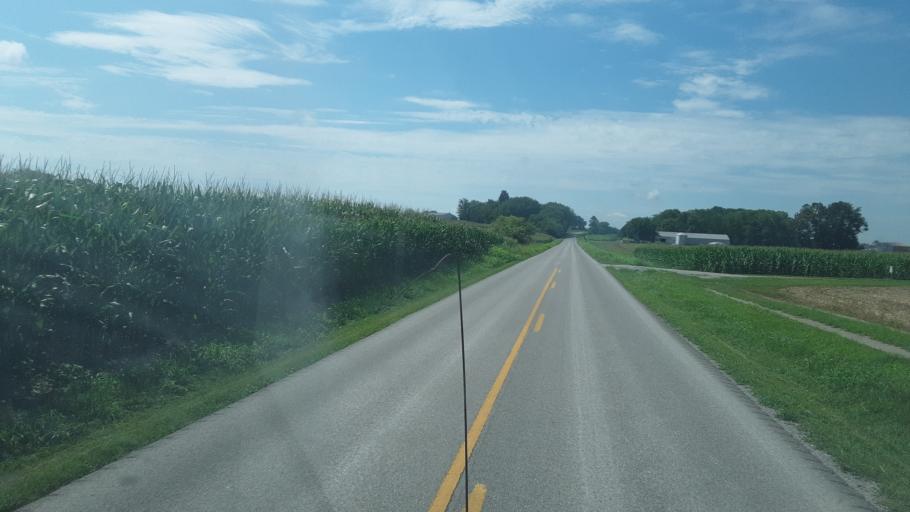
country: US
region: Kentucky
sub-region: Todd County
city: Elkton
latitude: 36.8174
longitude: -87.3144
